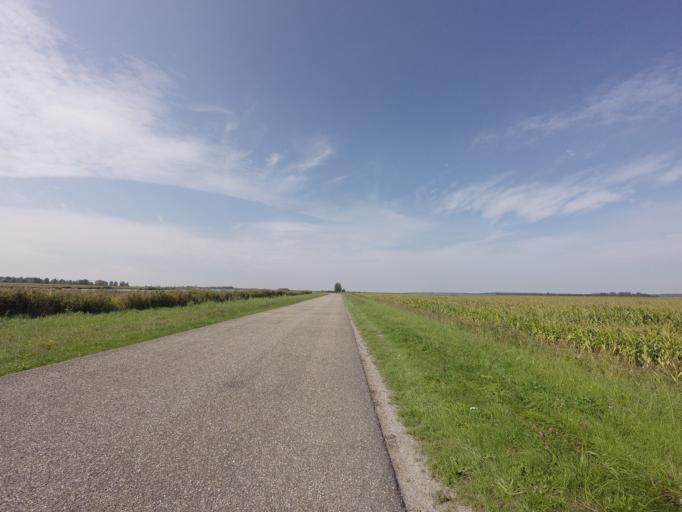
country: NL
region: Groningen
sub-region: Gemeente De Marne
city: Ulrum
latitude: 53.3455
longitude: 6.2755
